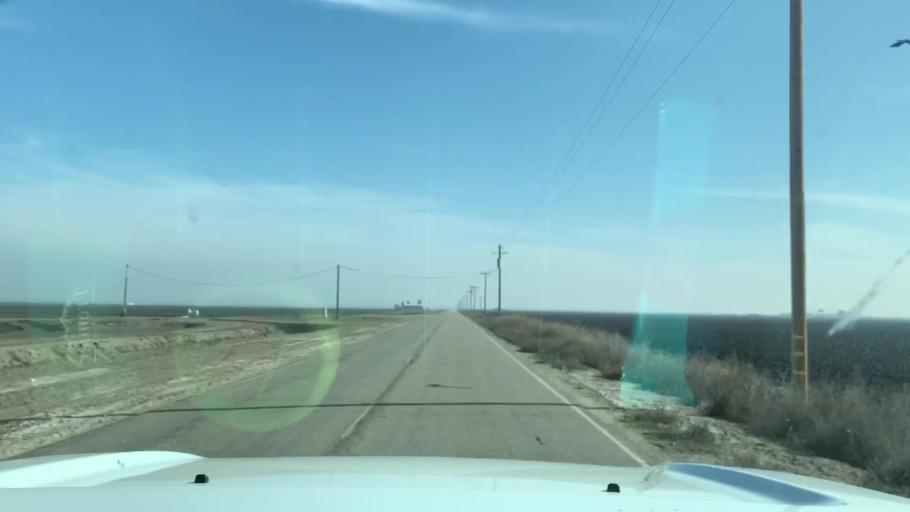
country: US
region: California
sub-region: Kern County
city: Buttonwillow
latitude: 35.4420
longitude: -119.5300
